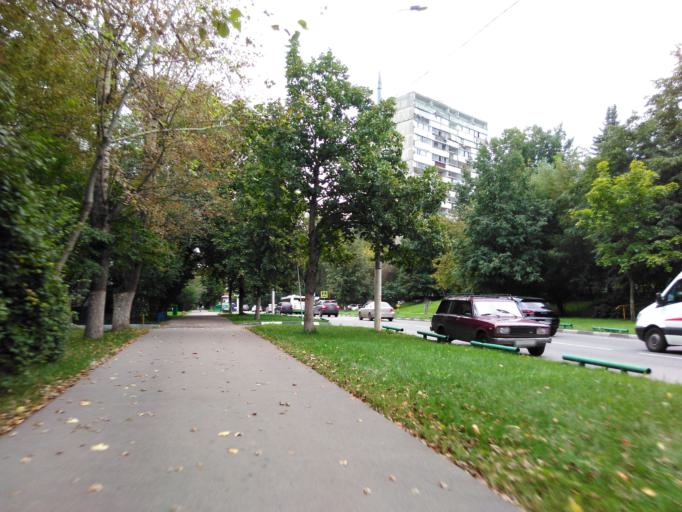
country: RU
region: Moscow
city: Zyuzino
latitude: 55.6623
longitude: 37.5839
